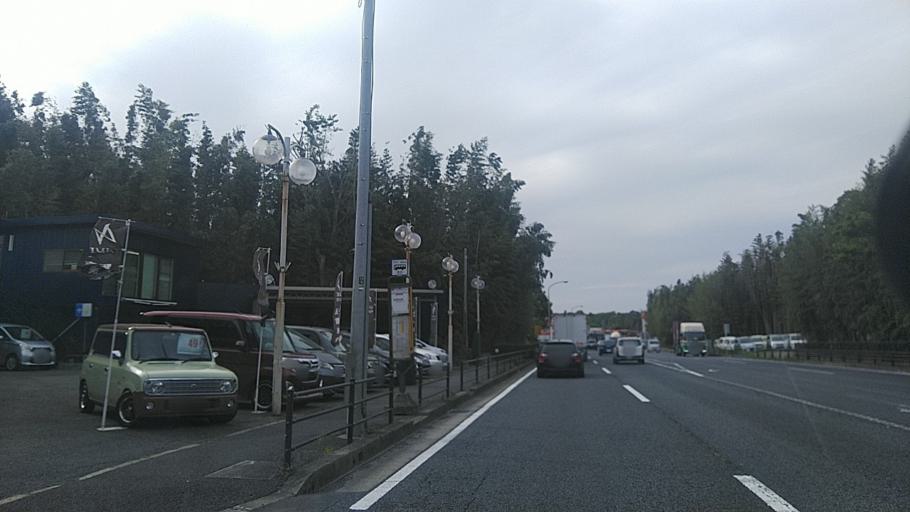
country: JP
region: Chiba
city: Yotsukaido
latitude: 35.6973
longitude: 140.1214
